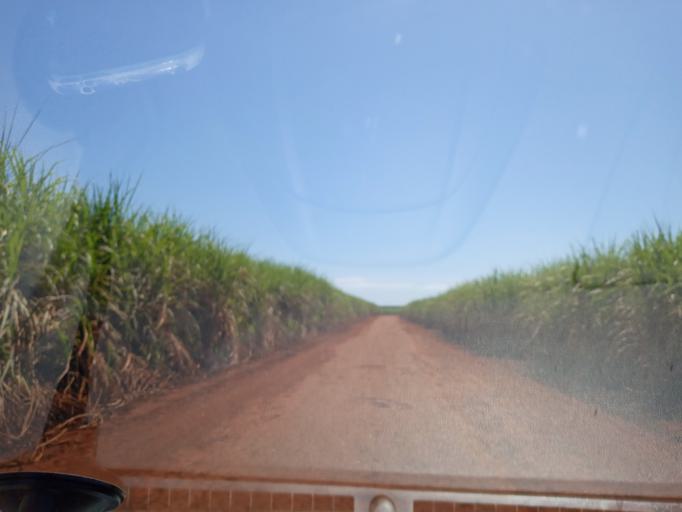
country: BR
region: Goias
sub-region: Itumbiara
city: Itumbiara
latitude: -18.4435
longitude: -49.1505
